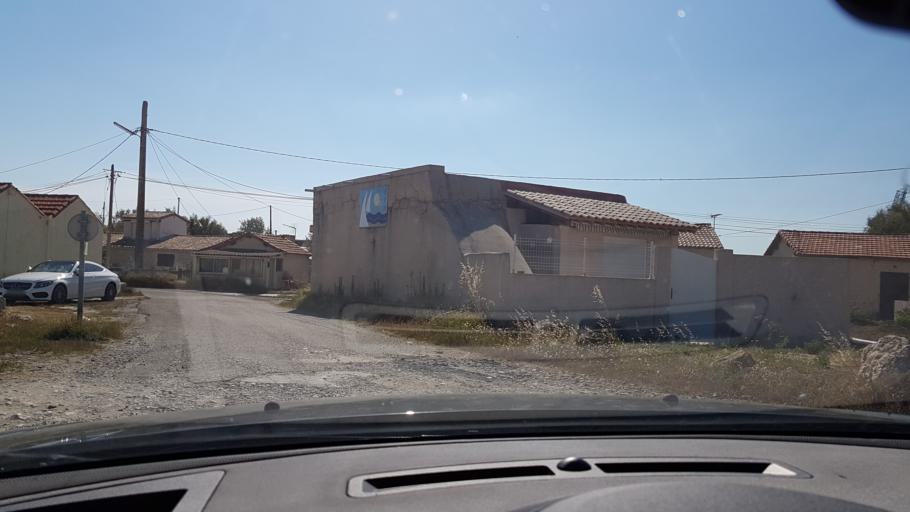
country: FR
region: Provence-Alpes-Cote d'Azur
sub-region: Departement des Bouches-du-Rhone
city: Port-Saint-Louis-du-Rhone
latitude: 43.3903
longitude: 4.8519
